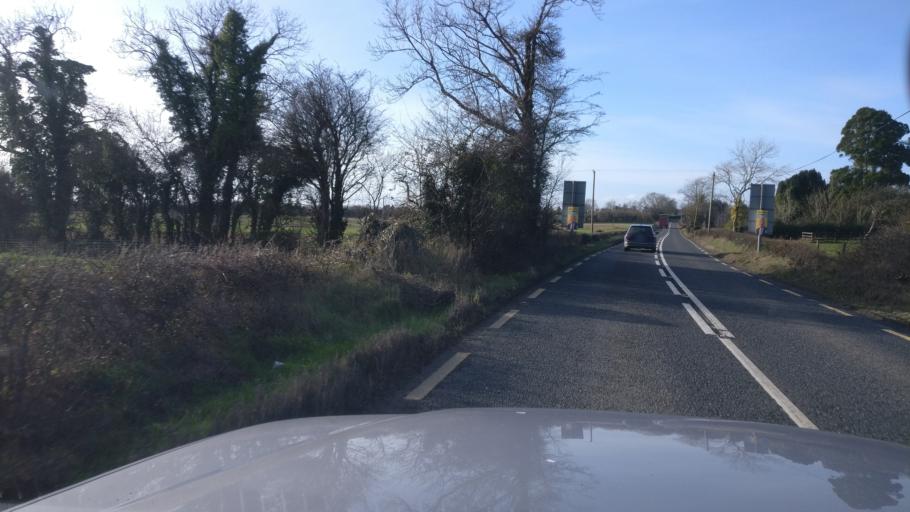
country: IE
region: Leinster
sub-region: Uibh Fhaili
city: Tullamore
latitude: 53.1980
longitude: -7.4222
